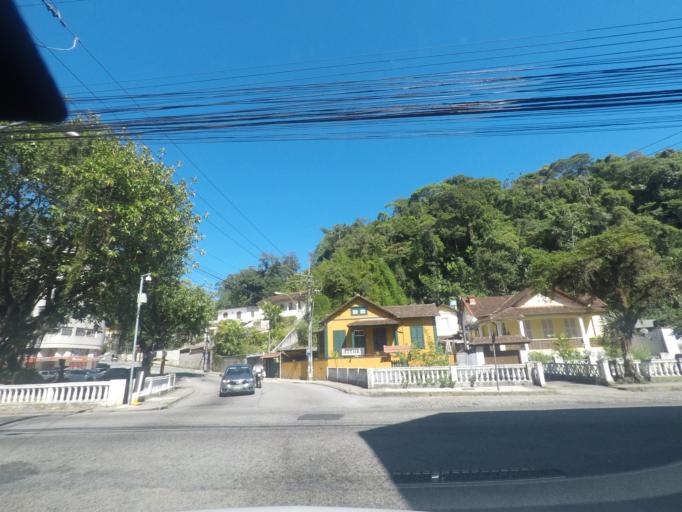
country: BR
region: Rio de Janeiro
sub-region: Petropolis
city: Petropolis
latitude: -22.5208
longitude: -43.1883
